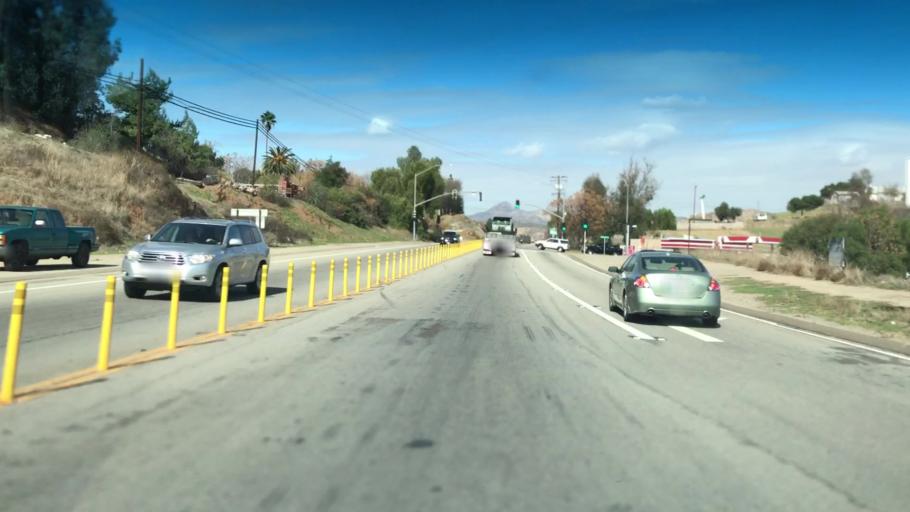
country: US
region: California
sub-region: San Diego County
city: Lakeside
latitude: 32.8724
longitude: -116.9239
